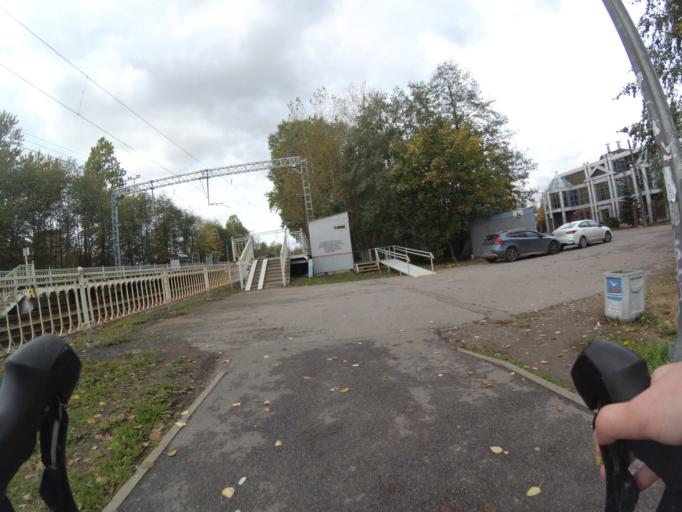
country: RU
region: St.-Petersburg
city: Lakhtinskiy
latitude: 59.9942
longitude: 30.1545
